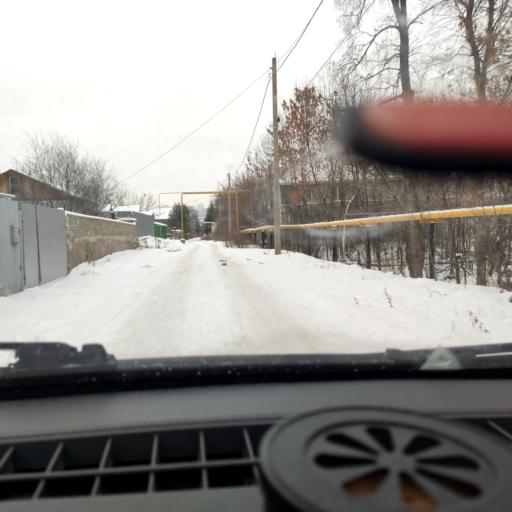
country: RU
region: Bashkortostan
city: Ufa
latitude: 54.7072
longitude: 55.9435
